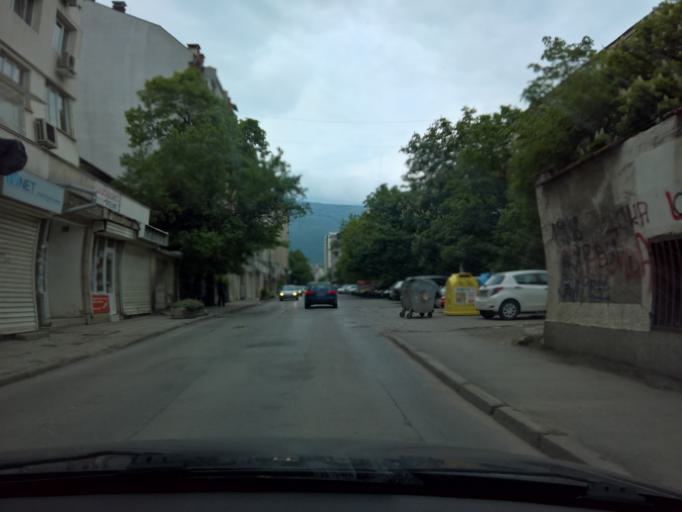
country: BG
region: Sofia-Capital
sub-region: Stolichna Obshtina
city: Sofia
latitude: 42.6624
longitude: 23.3021
